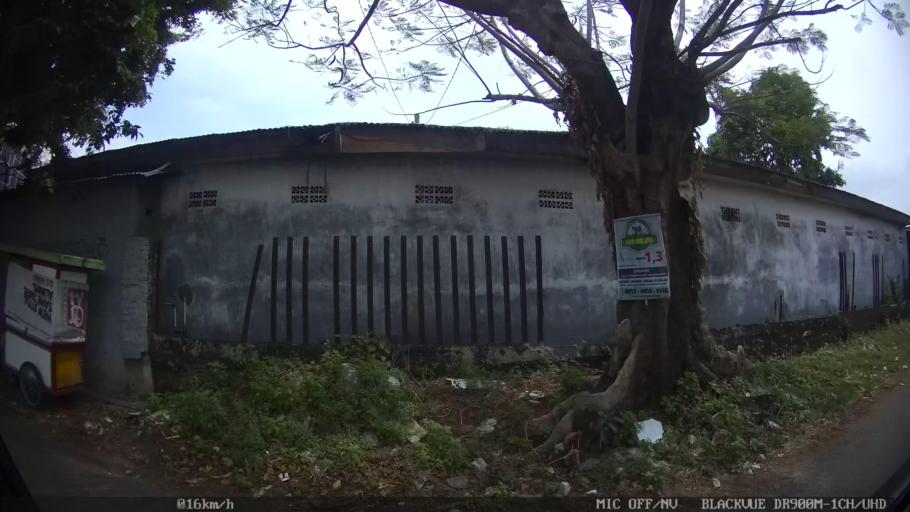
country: ID
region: Lampung
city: Bandarlampung
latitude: -5.4201
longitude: 105.2689
